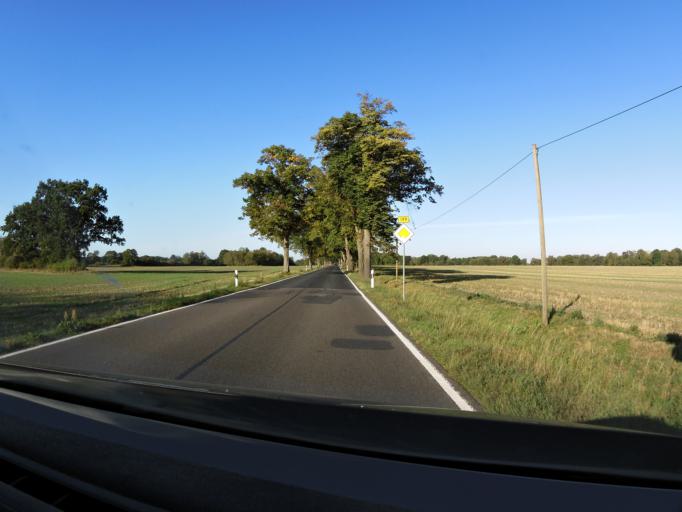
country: DE
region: Mecklenburg-Vorpommern
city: Alt-Sanitz
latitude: 53.8277
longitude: 13.5381
